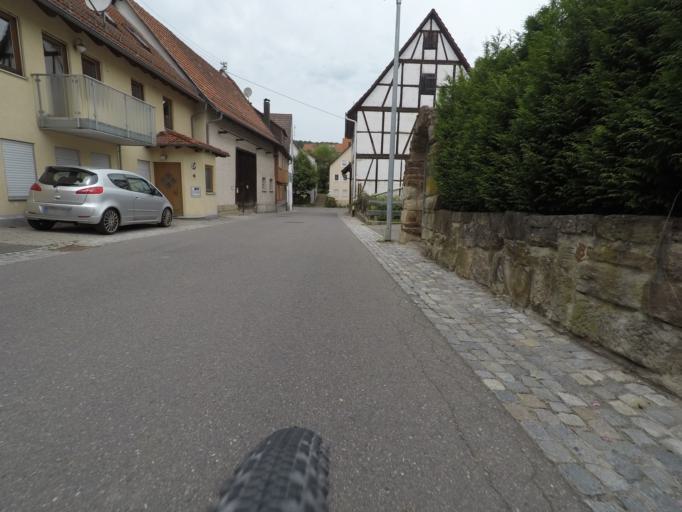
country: DE
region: Baden-Wuerttemberg
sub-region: Regierungsbezirk Stuttgart
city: Hildrizhausen
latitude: 48.5706
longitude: 8.9584
